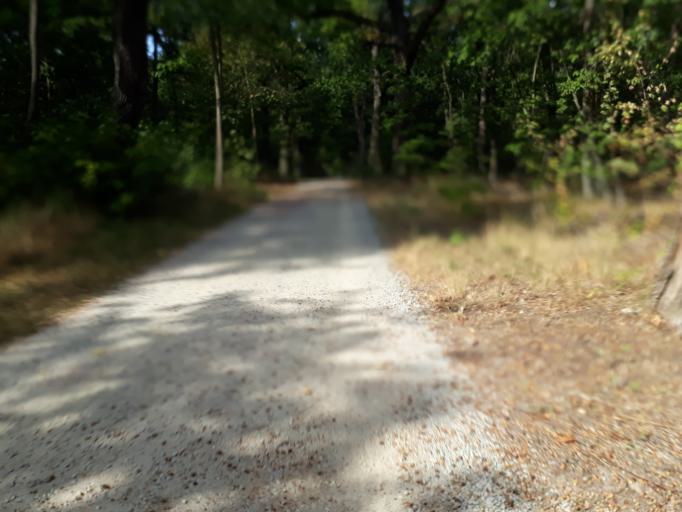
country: DE
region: Berlin
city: Grunewald
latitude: 52.4844
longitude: 13.2315
